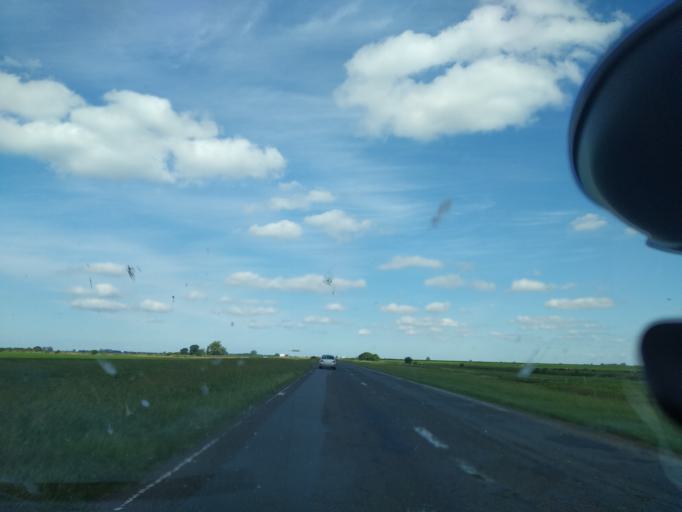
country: AR
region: Santa Fe
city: Roldan
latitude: -32.9032
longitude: -61.0202
